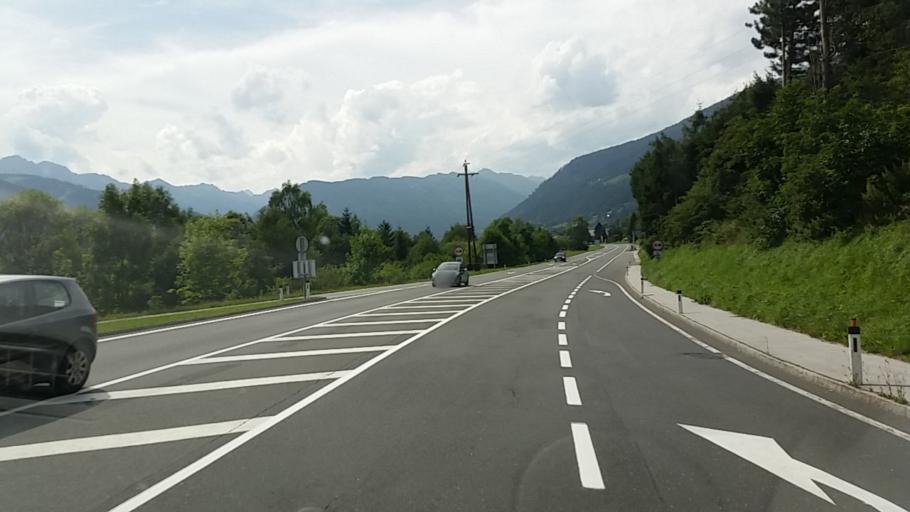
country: AT
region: Salzburg
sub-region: Politischer Bezirk Tamsweg
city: Sankt Margarethen im Lungau
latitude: 47.0932
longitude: 13.6784
